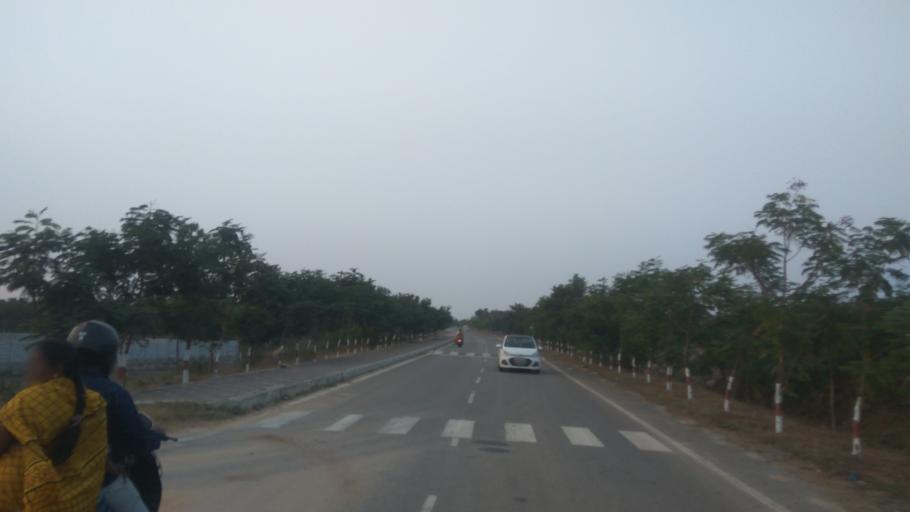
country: IN
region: Telangana
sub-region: Rangareddi
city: Secunderabad
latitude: 17.5588
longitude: 78.6263
